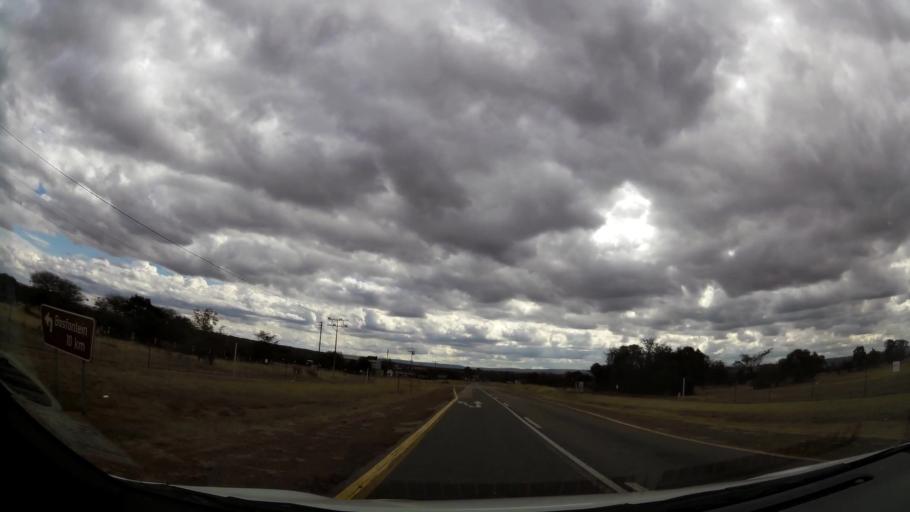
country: ZA
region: Limpopo
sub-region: Waterberg District Municipality
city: Modimolle
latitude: -24.7544
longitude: 28.4497
